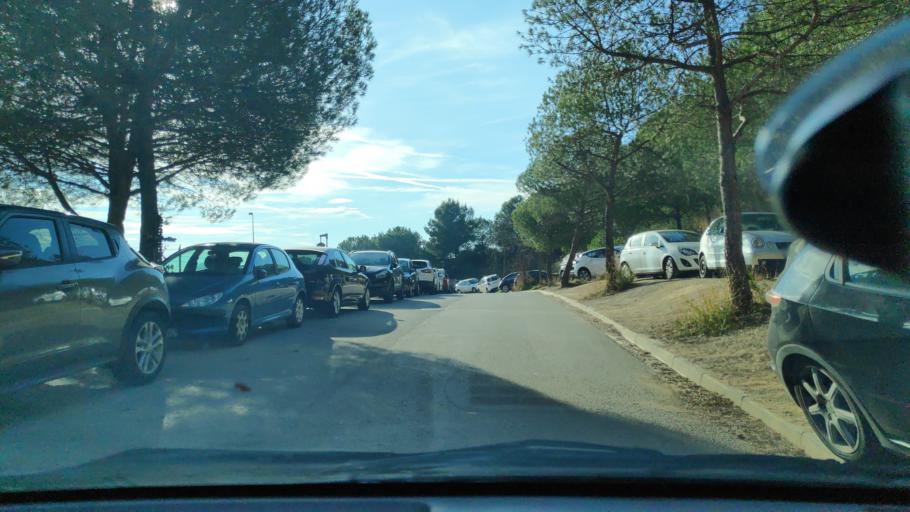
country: ES
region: Catalonia
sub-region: Provincia de Barcelona
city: Rubi
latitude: 41.4932
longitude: 2.0548
